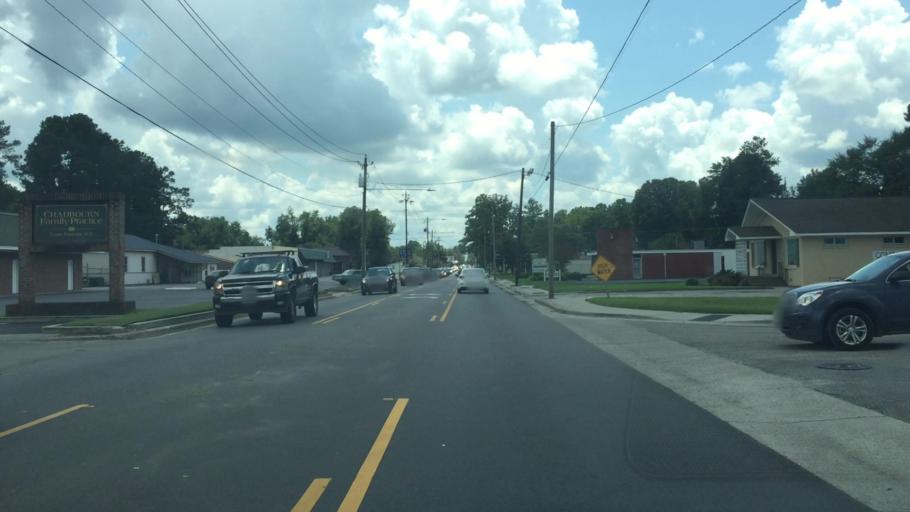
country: US
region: North Carolina
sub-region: Columbus County
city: Chadbourn
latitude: 34.3297
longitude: -78.8265
